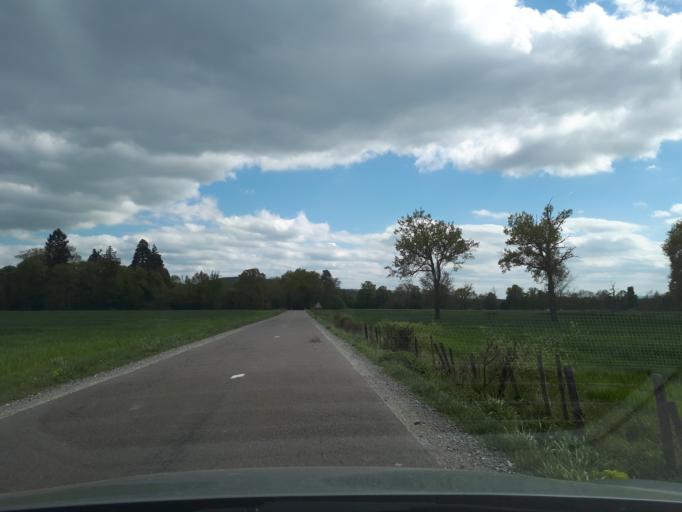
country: FR
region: Rhone-Alpes
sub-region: Departement de la Loire
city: Bellegarde-en-Forez
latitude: 45.7164
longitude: 4.2959
